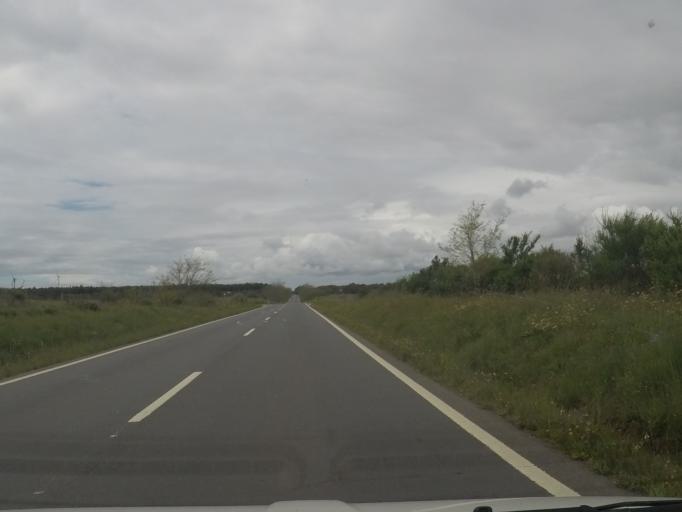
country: PT
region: Setubal
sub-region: Santiago do Cacem
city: Cercal
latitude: 37.8418
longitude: -8.7045
